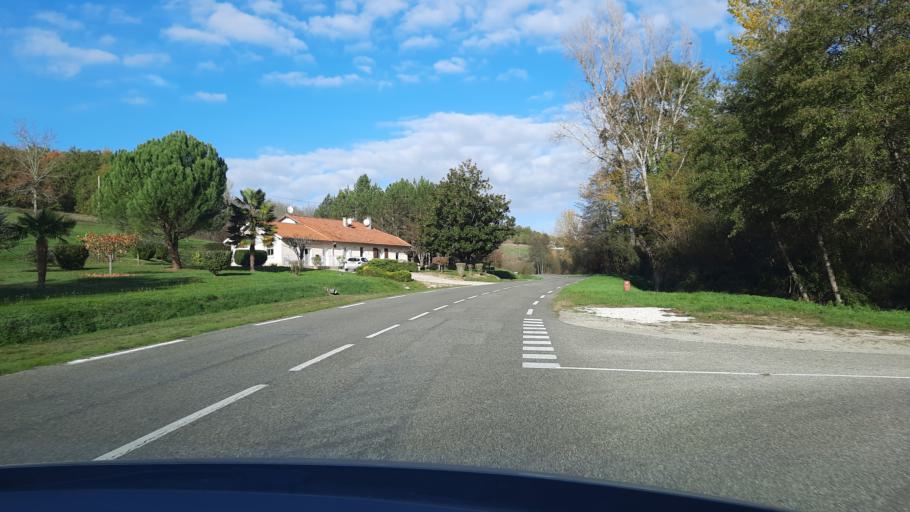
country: FR
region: Midi-Pyrenees
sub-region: Departement du Tarn-et-Garonne
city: Molieres
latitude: 44.1131
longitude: 1.3559
